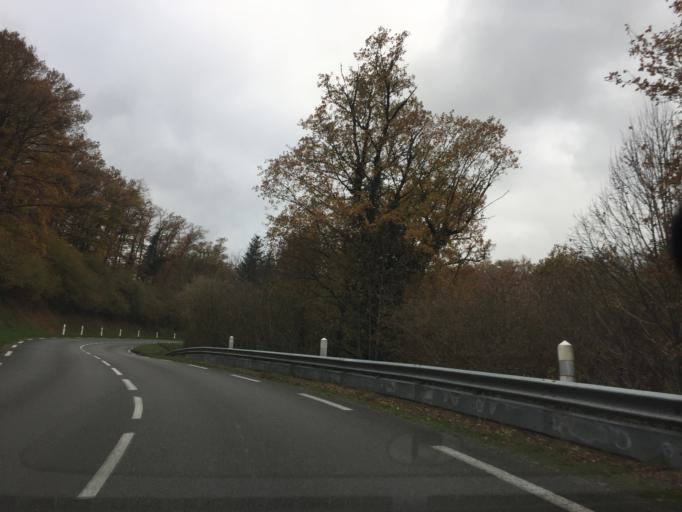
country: FR
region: Limousin
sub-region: Departement de la Creuse
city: Ahun
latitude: 46.0856
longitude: 2.0595
